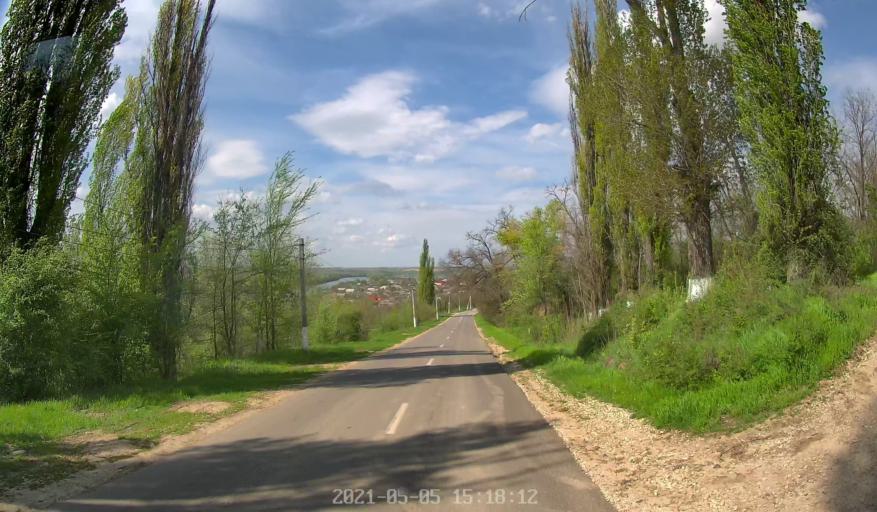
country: MD
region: Criuleni
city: Criuleni
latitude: 47.1178
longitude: 29.1942
